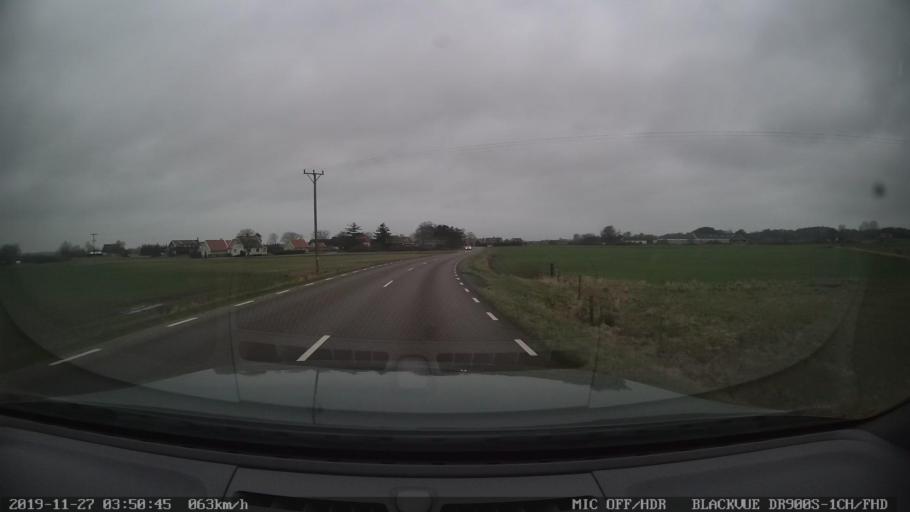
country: SE
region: Skane
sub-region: Hoganas Kommun
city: Hoganas
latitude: 56.2502
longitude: 12.5671
